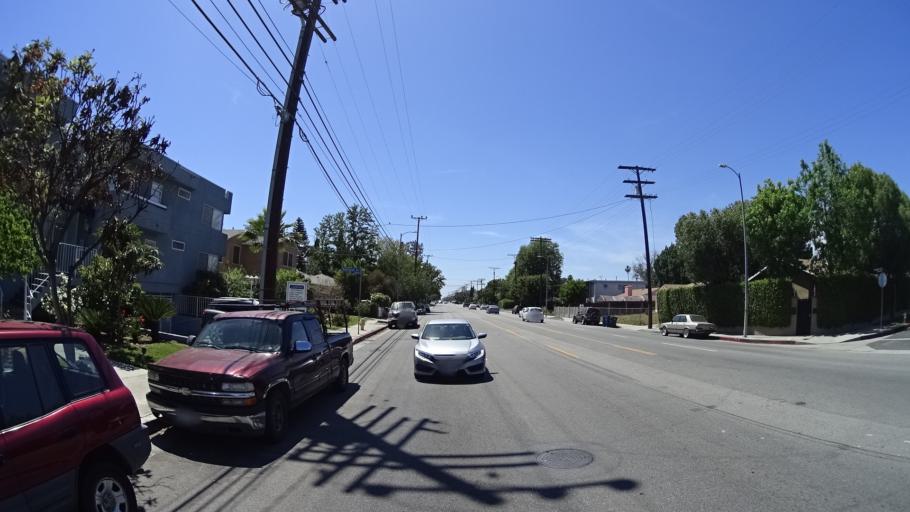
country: US
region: California
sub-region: Los Angeles County
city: North Hollywood
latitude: 34.1794
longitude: -118.3989
